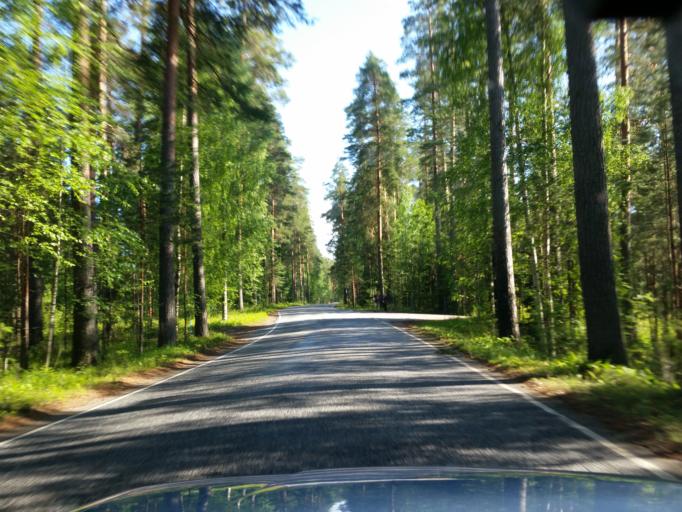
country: FI
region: Southern Savonia
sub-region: Savonlinna
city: Sulkava
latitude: 61.7875
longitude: 28.4251
